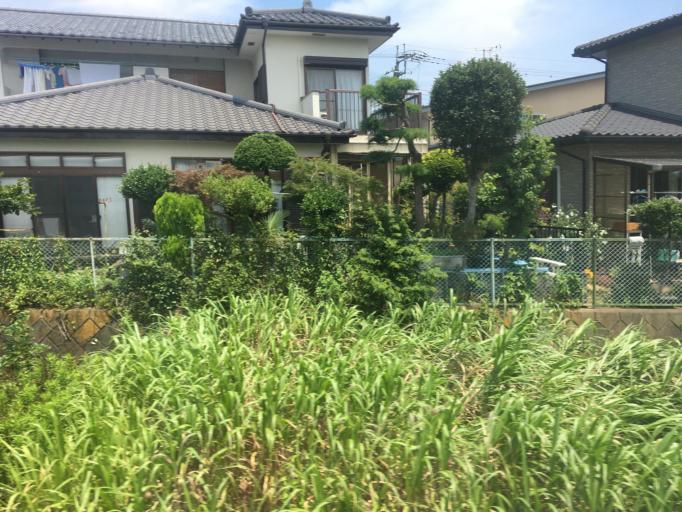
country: JP
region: Gunma
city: Ota
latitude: 36.2844
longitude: 139.4022
